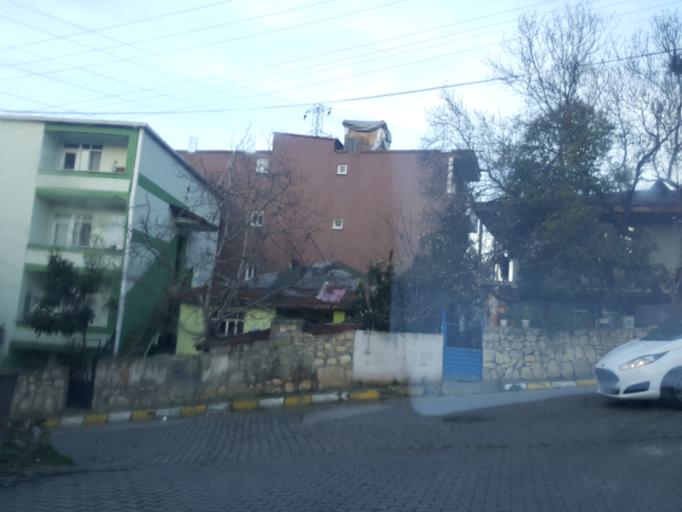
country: TR
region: Kocaeli
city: Tavsancil
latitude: 40.7862
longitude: 29.5459
